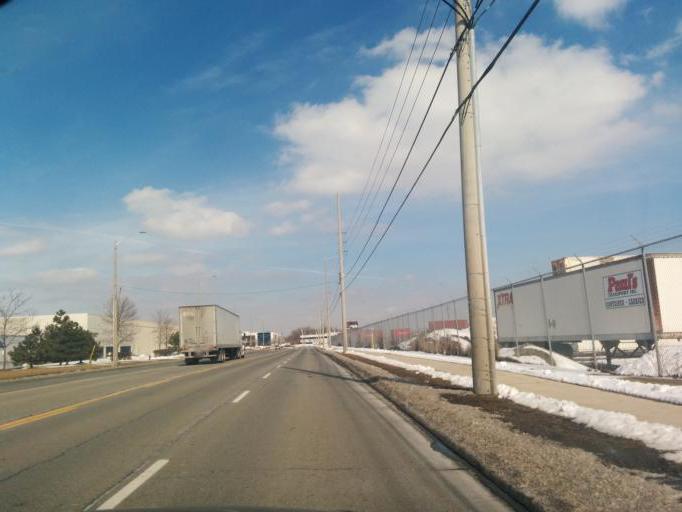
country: CA
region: Ontario
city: Etobicoke
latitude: 43.6447
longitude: -79.6270
